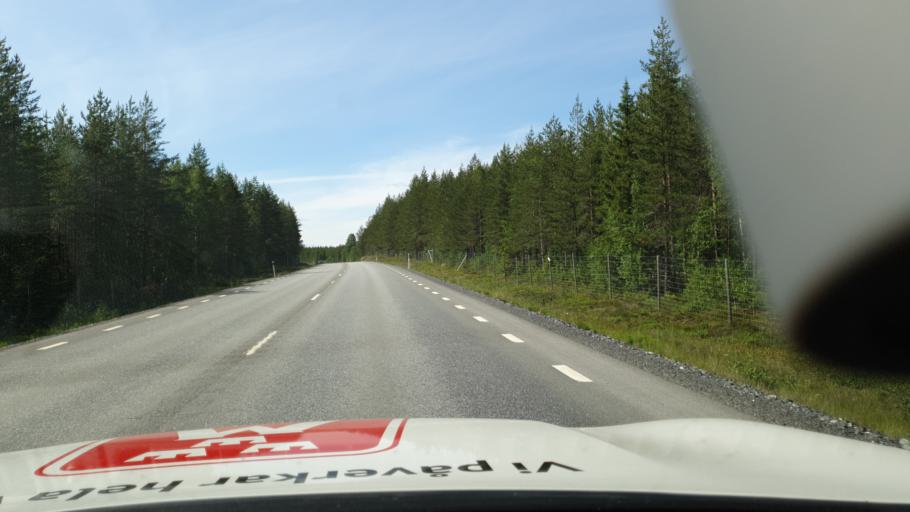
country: SE
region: Vaesterbotten
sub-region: Skelleftea Kommun
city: Forsbacka
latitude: 64.8246
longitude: 20.5849
